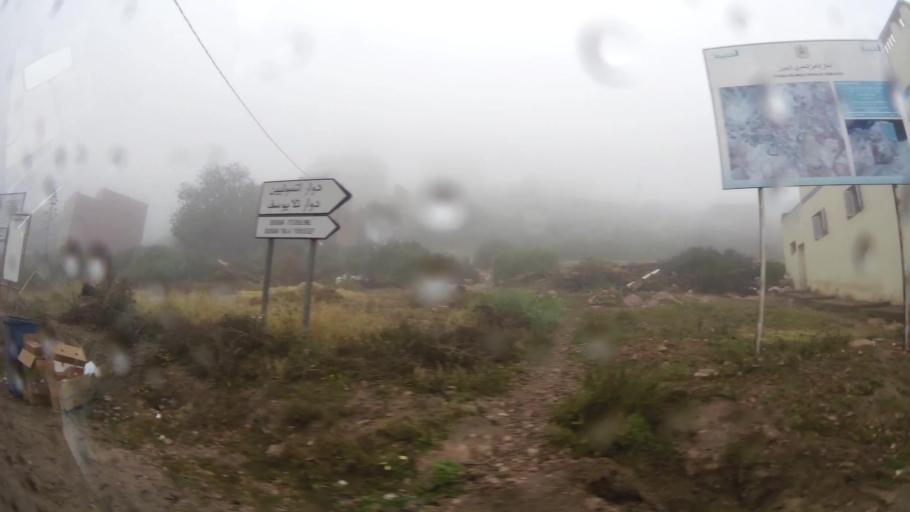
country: MA
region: Taza-Al Hoceima-Taounate
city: Tirhanimine
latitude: 35.2296
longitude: -3.9720
